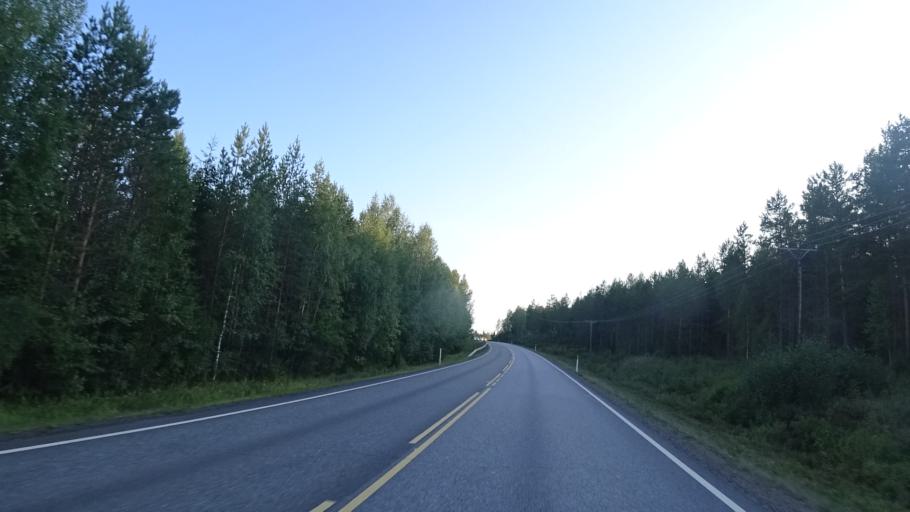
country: FI
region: South Karelia
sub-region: Lappeenranta
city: Ylaemaa
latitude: 60.8465
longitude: 28.1206
